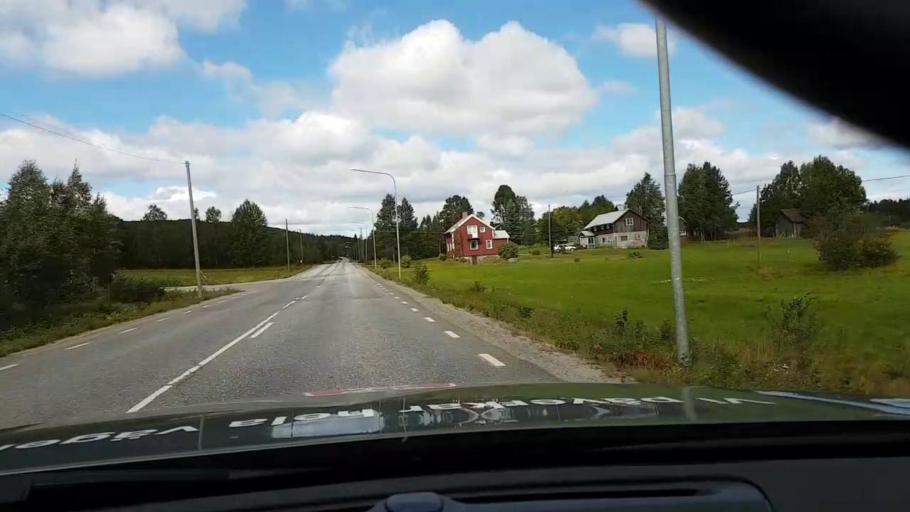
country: SE
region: Vaesternorrland
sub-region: OErnskoeldsviks Kommun
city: Bredbyn
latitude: 63.4811
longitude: 18.0909
